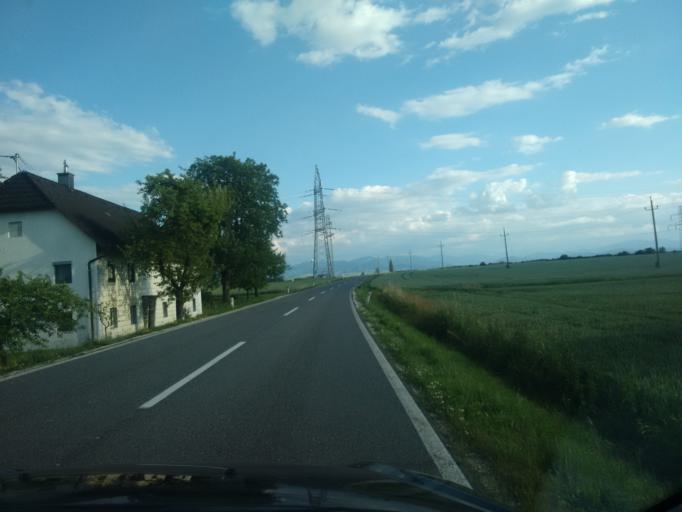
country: AT
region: Upper Austria
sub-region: Politischer Bezirk Steyr-Land
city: Sierning
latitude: 48.0937
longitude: 14.3189
